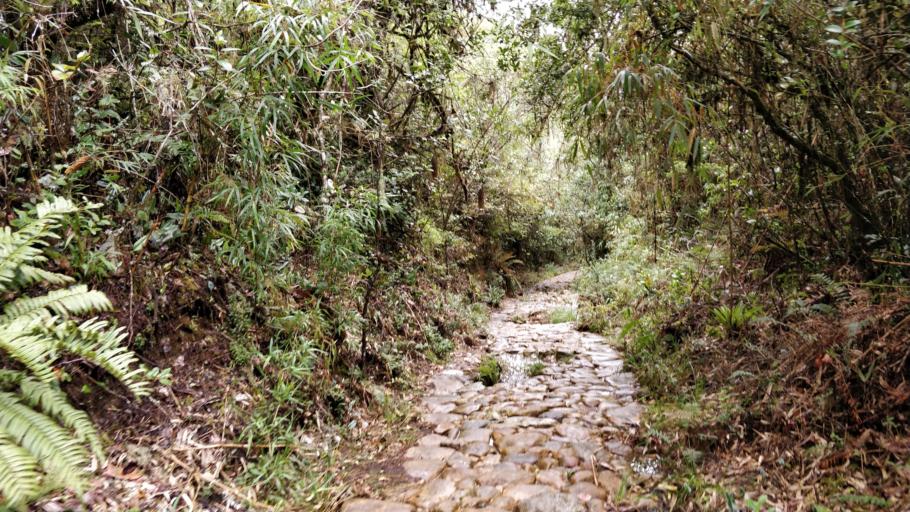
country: CO
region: Bogota D.C.
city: Bogota
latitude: 4.5401
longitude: -74.0531
